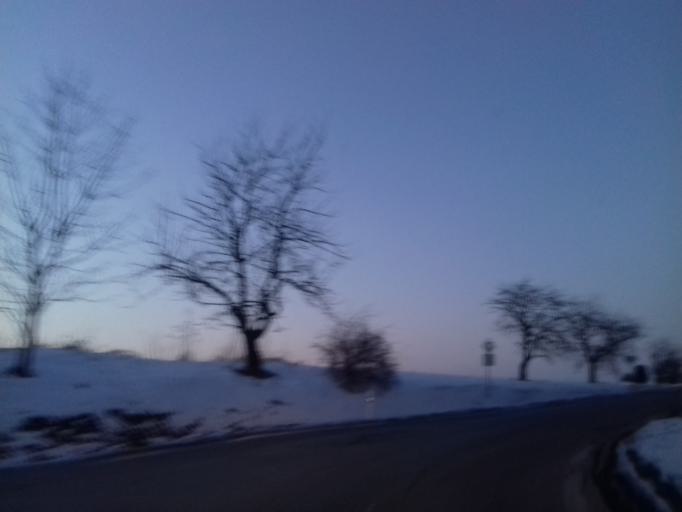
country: CZ
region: Central Bohemia
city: Rudna
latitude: 50.0325
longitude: 14.2644
